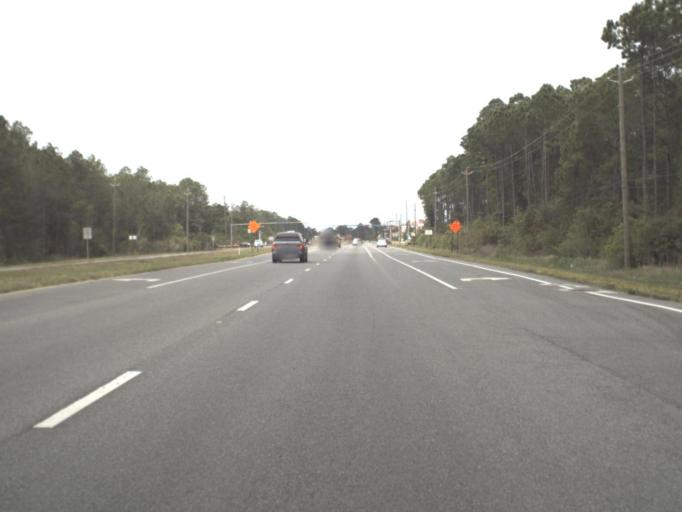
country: US
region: Florida
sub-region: Escambia County
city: Myrtle Grove
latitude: 30.4006
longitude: -87.3147
